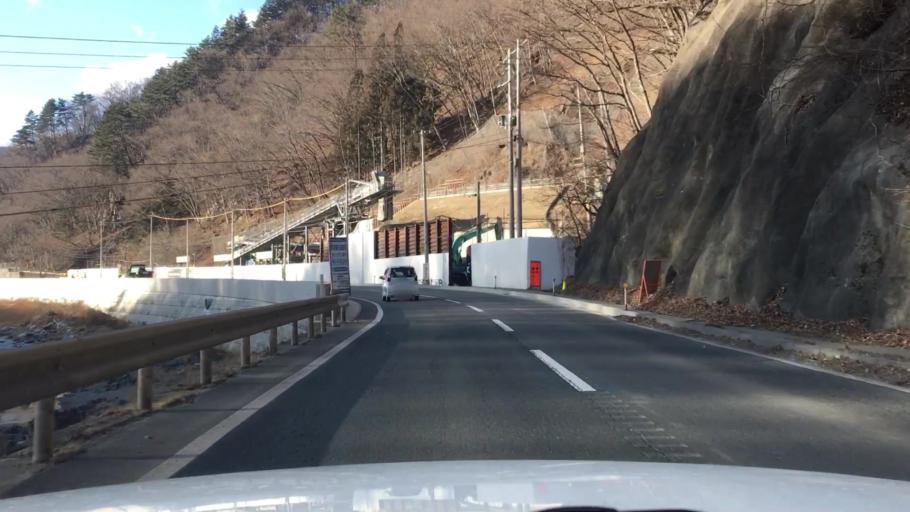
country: JP
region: Iwate
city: Miyako
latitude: 39.6011
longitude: 141.7114
